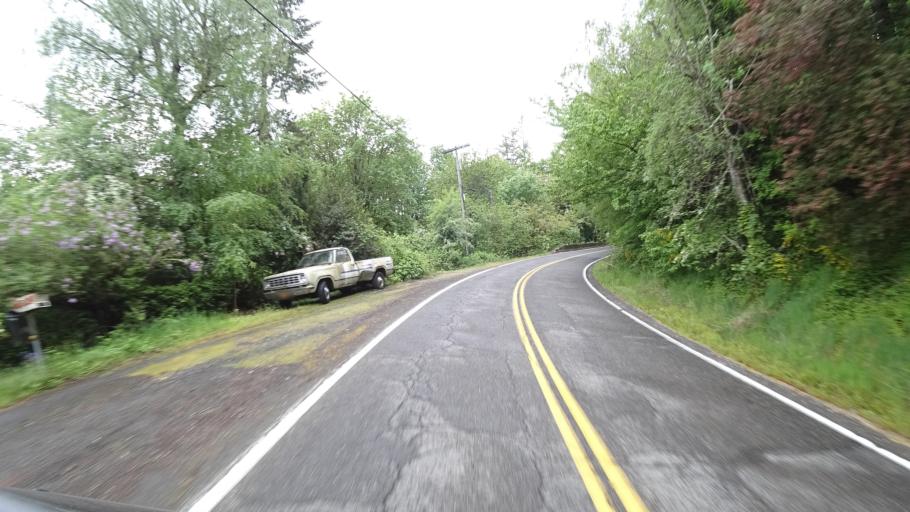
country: US
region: Oregon
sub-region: Washington County
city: West Haven
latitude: 45.5418
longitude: -122.7483
